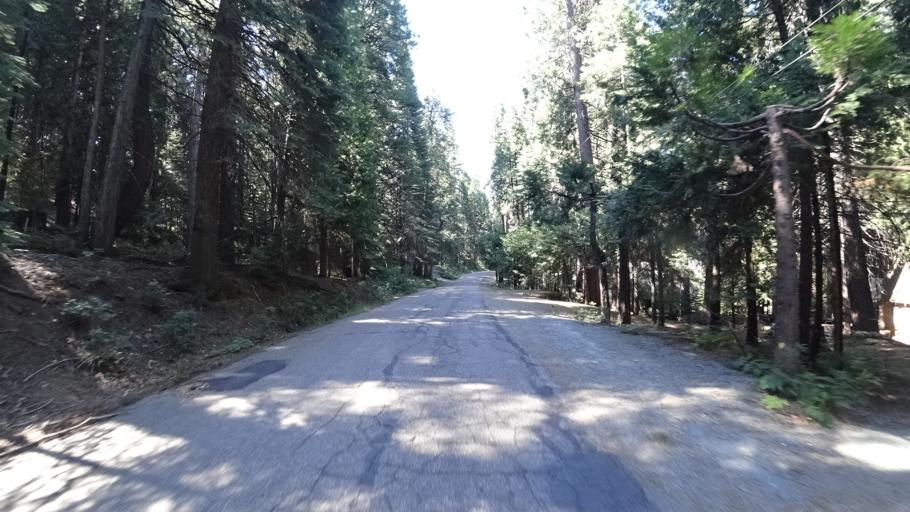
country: US
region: California
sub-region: Calaveras County
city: Arnold
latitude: 38.2966
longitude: -120.2729
